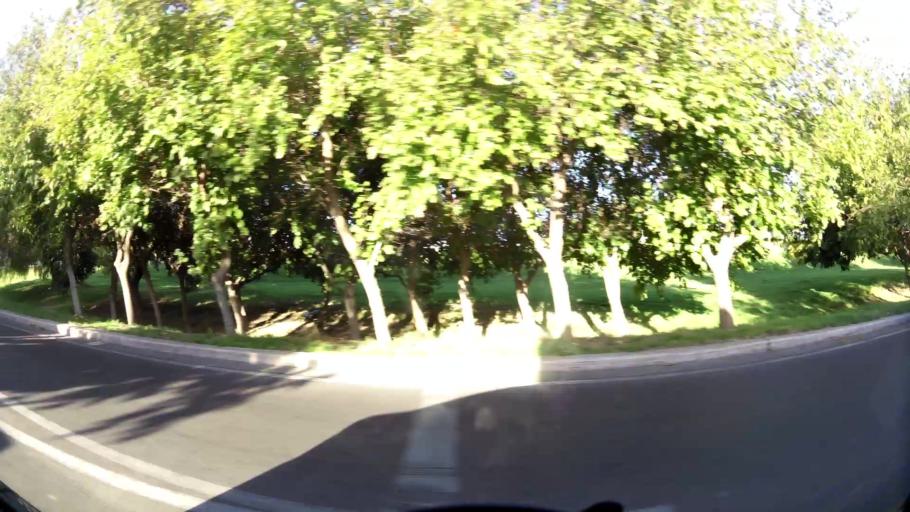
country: AR
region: San Juan
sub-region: Departamento de Santa Lucia
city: Santa Lucia
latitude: -31.5408
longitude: -68.5043
